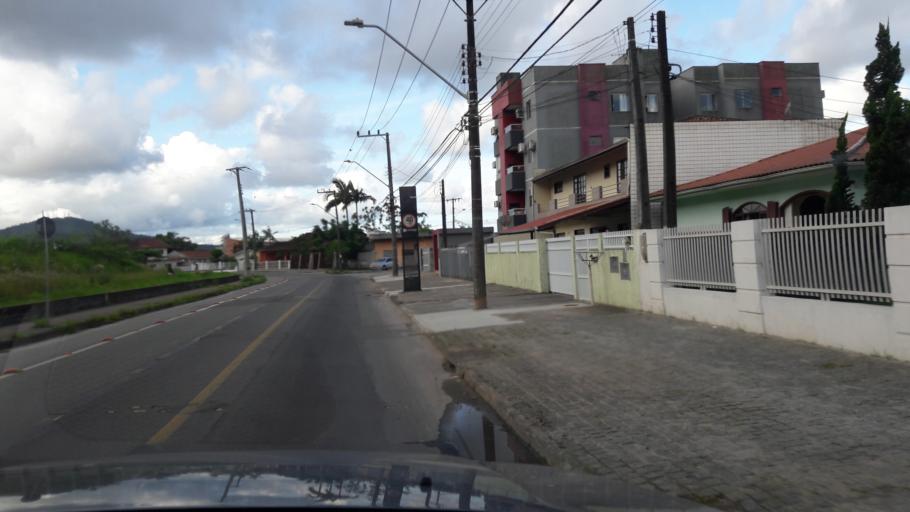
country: BR
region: Santa Catarina
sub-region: Joinville
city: Joinville
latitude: -26.3241
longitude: -48.8222
